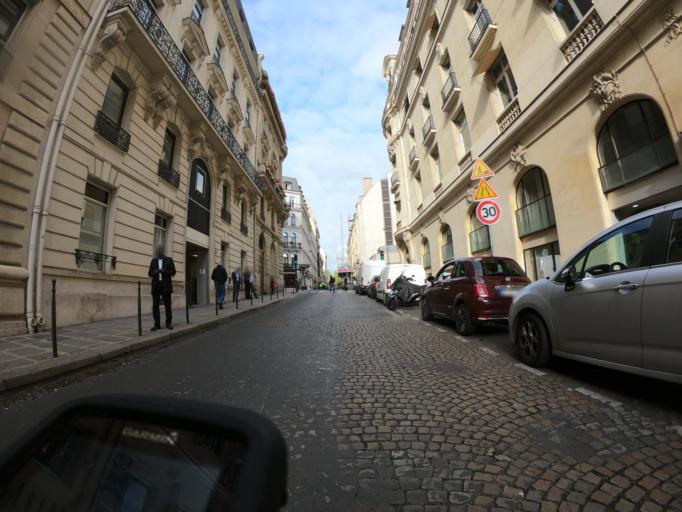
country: FR
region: Ile-de-France
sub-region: Departement des Hauts-de-Seine
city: Levallois-Perret
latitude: 48.8717
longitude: 2.2993
